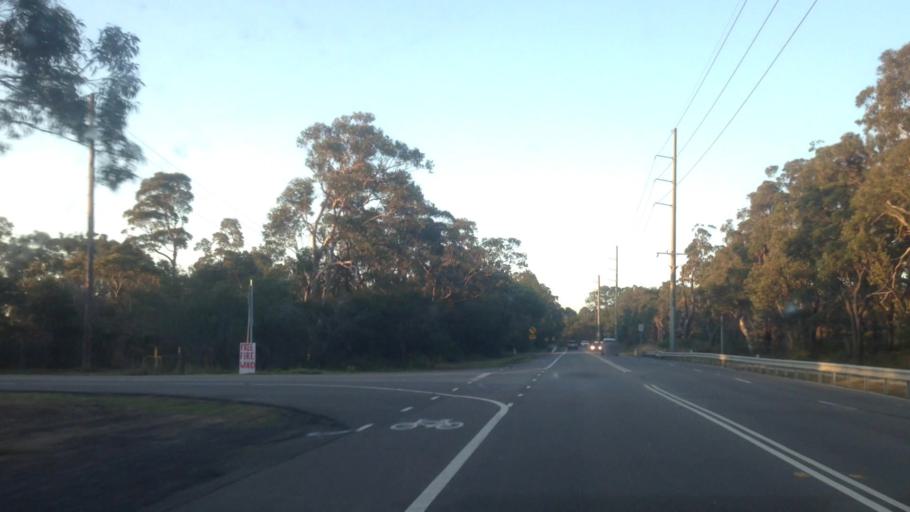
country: AU
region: New South Wales
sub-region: Wyong Shire
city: Kingfisher Shores
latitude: -33.1802
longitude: 151.5391
